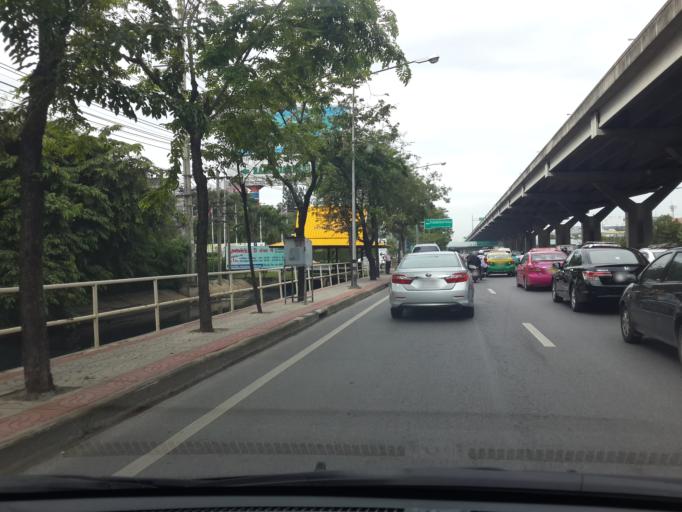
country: TH
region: Bangkok
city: Lak Si
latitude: 13.8639
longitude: 100.5706
